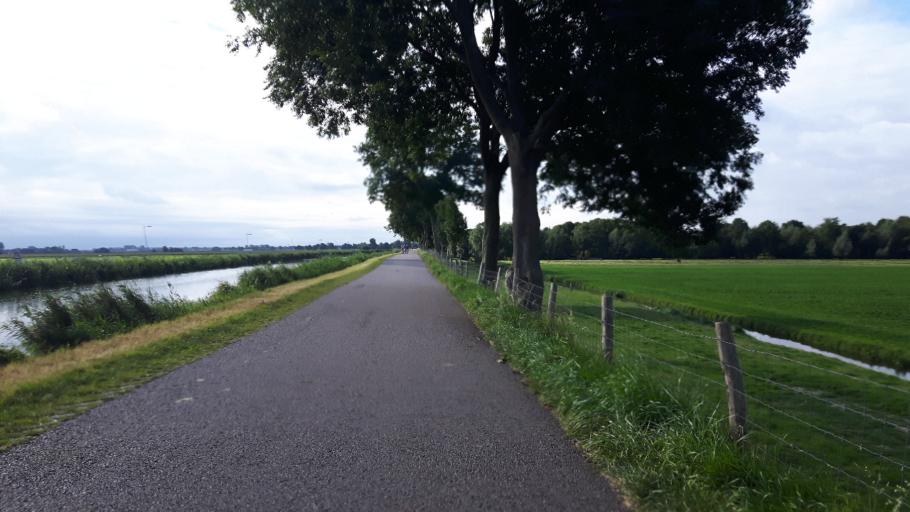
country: NL
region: North Holland
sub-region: Gemeente Purmerend
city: Purmerend
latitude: 52.5576
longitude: 4.9767
